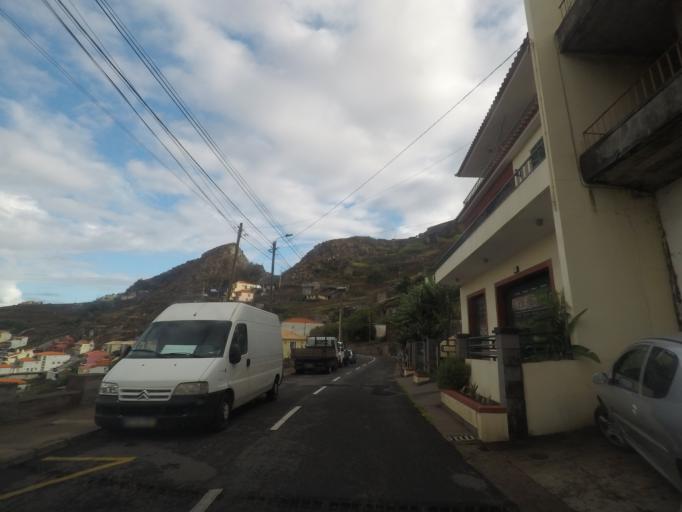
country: PT
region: Madeira
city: Camara de Lobos
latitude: 32.6575
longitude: -16.9971
